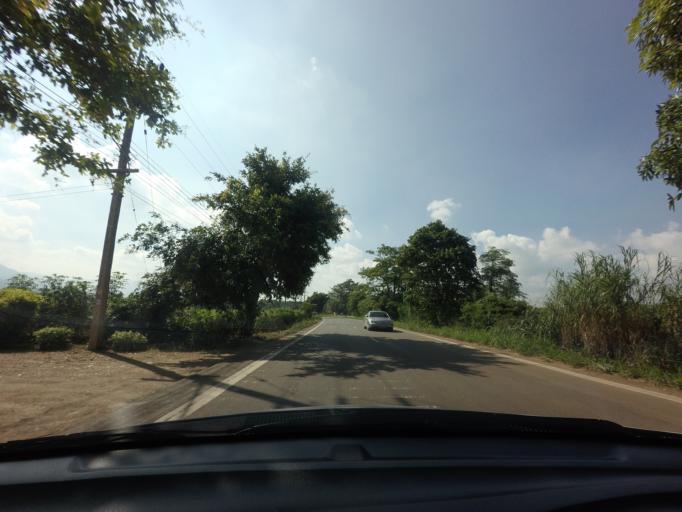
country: TH
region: Nakhon Ratchasima
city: Wang Nam Khiao
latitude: 14.4672
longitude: 101.6359
